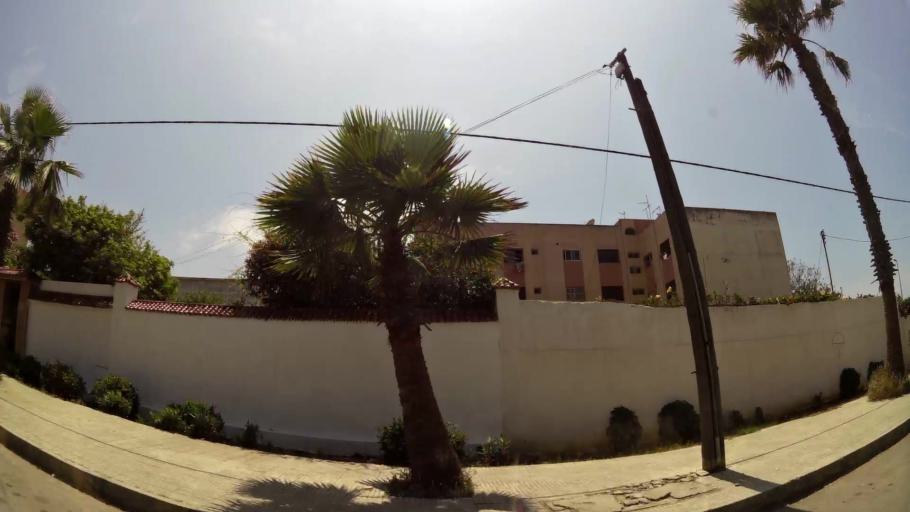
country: MA
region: Rabat-Sale-Zemmour-Zaer
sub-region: Rabat
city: Rabat
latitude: 34.0168
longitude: -6.8560
